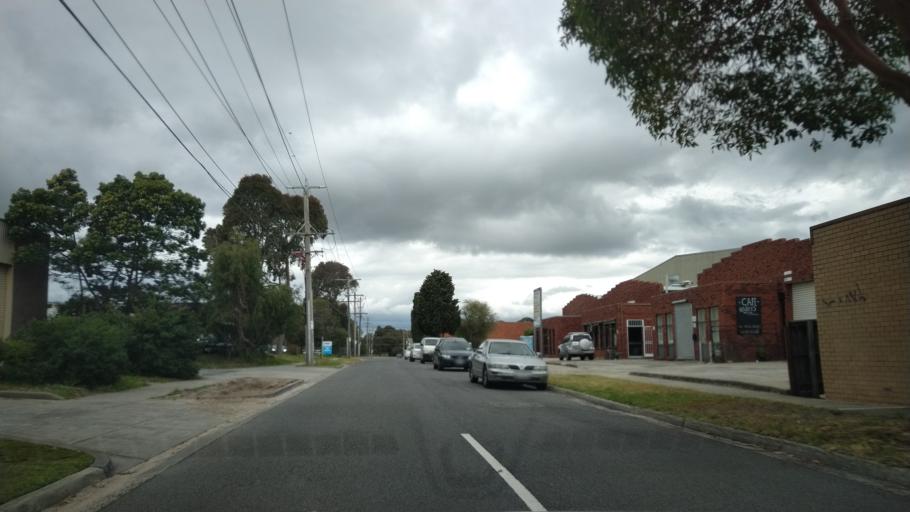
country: AU
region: Victoria
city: Highett
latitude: -37.9562
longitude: 145.0731
